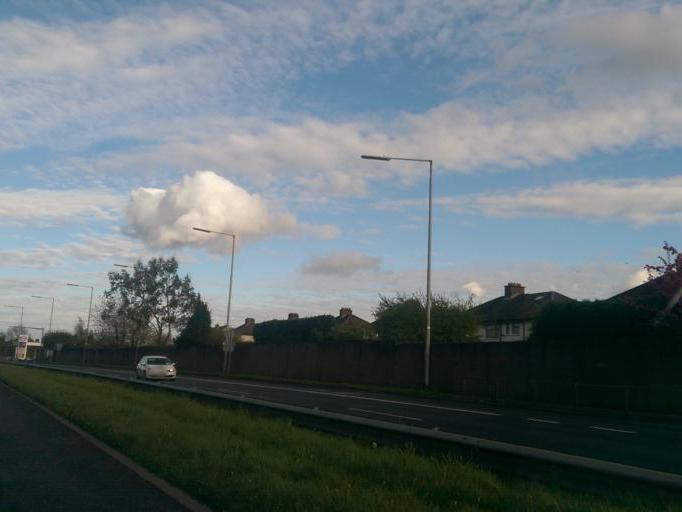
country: IE
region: Leinster
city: Ballyfermot
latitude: 53.3537
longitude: -6.3665
